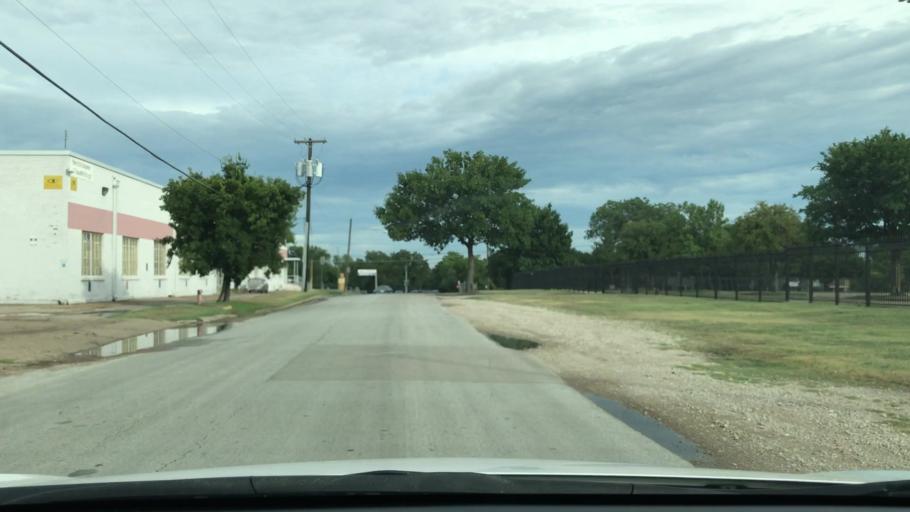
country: US
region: Texas
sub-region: Dallas County
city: Dallas
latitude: 32.7789
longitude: -96.7517
